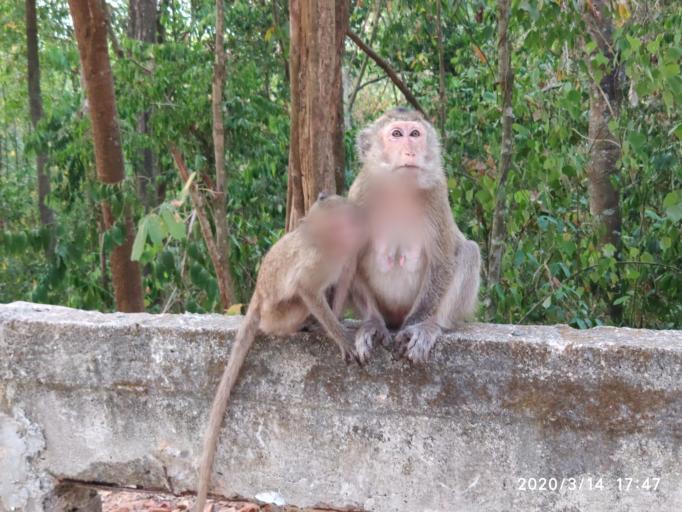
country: TH
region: Rayong
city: Klaeng
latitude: 12.6495
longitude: 101.5318
